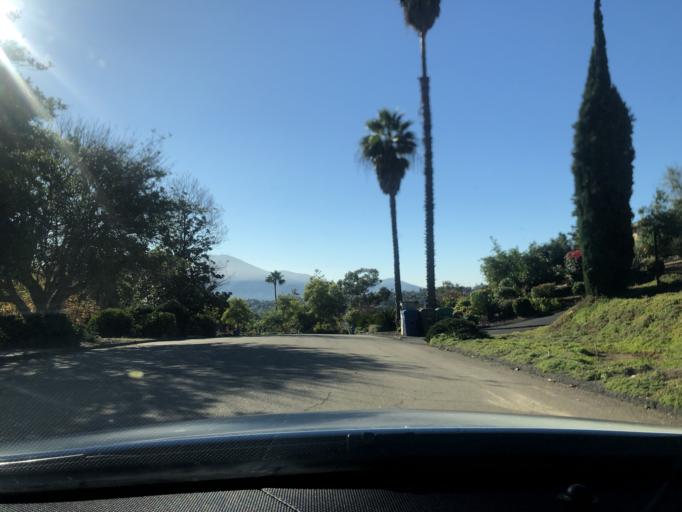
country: US
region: California
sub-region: San Diego County
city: Casa de Oro-Mount Helix
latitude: 32.7681
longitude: -116.9487
